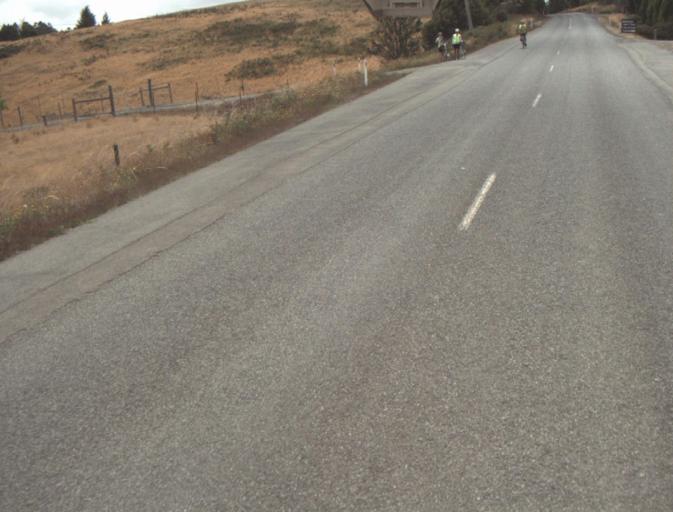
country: AU
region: Tasmania
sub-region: Launceston
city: Mayfield
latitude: -41.2098
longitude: 147.2138
